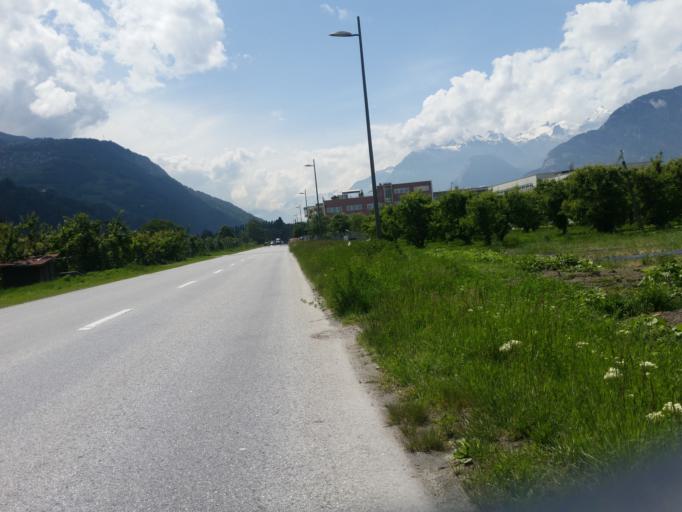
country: CH
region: Valais
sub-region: Sion District
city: Sitten
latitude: 46.2187
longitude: 7.3451
